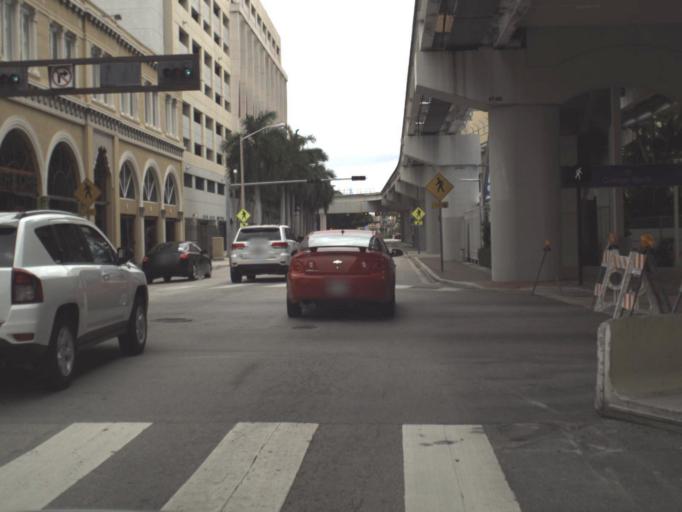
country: US
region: Florida
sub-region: Miami-Dade County
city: Miami
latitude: 25.7790
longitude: -80.1922
